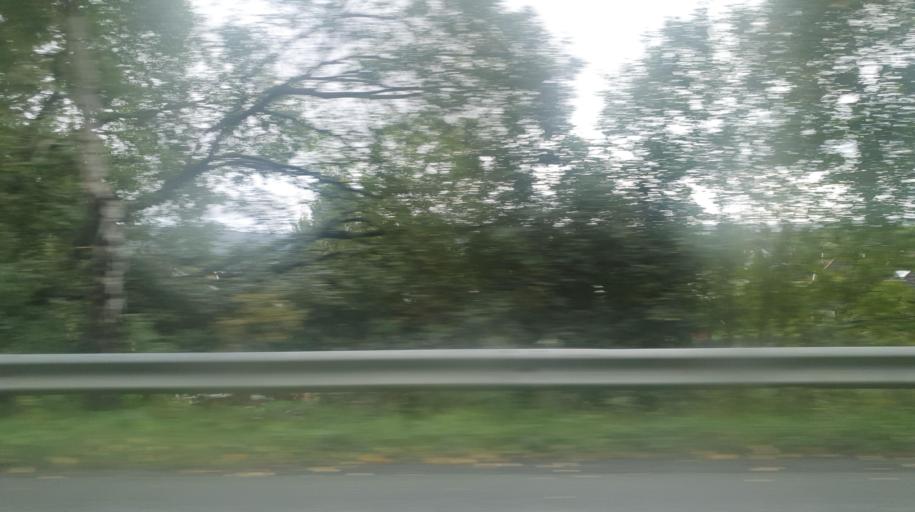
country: NO
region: Nord-Trondelag
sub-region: Verdal
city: Verdal
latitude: 63.7956
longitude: 11.5134
